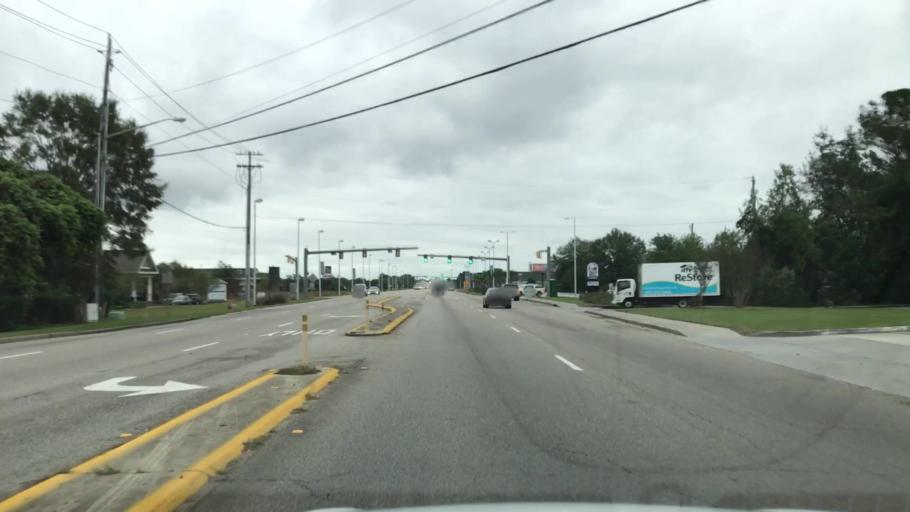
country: US
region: South Carolina
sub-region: Georgetown County
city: Georgetown
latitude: 33.3676
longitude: -79.2741
